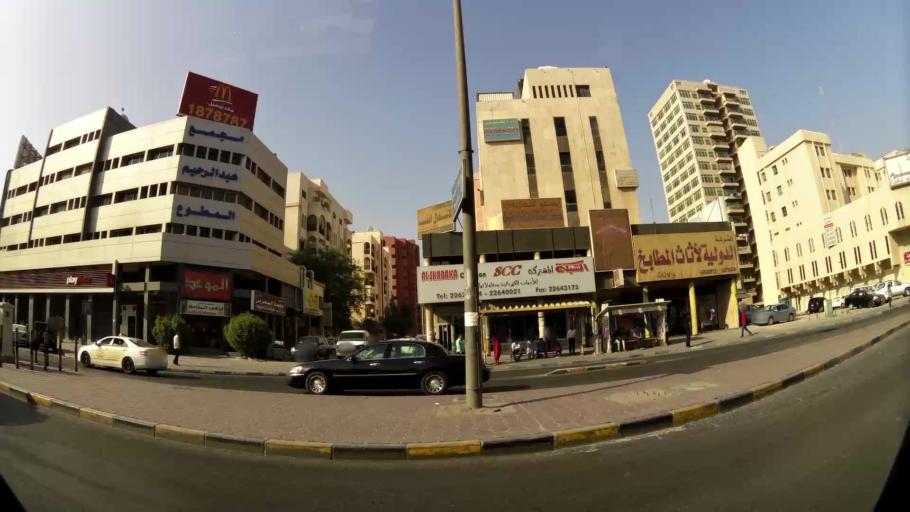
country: KW
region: Muhafazat Hawalli
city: Hawalli
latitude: 29.3332
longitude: 48.0267
